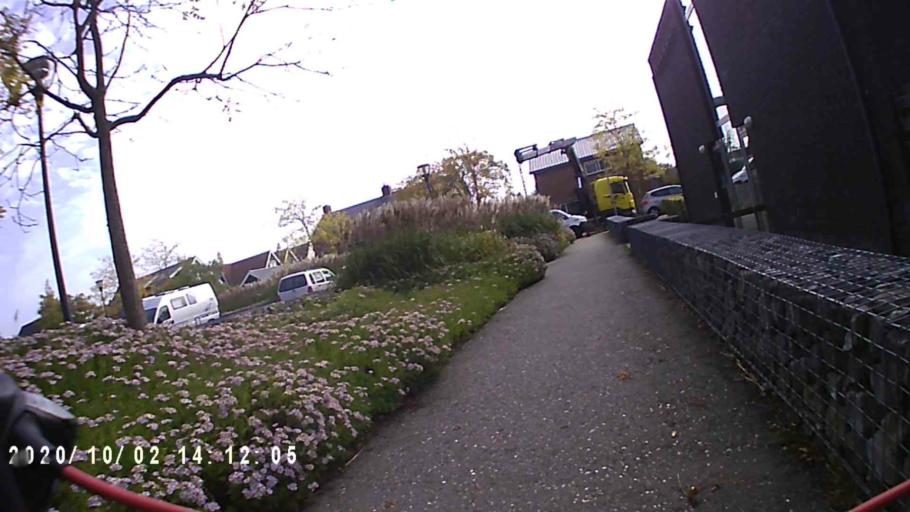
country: NL
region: Groningen
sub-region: Gemeente Zuidhorn
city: Zuidhorn
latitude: 53.2444
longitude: 6.4033
